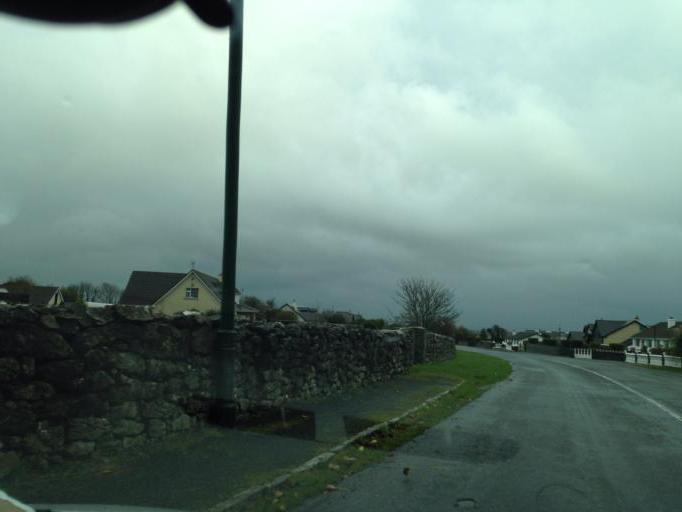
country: IE
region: Connaught
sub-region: County Galway
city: Oranmore
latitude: 53.2722
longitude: -8.9794
